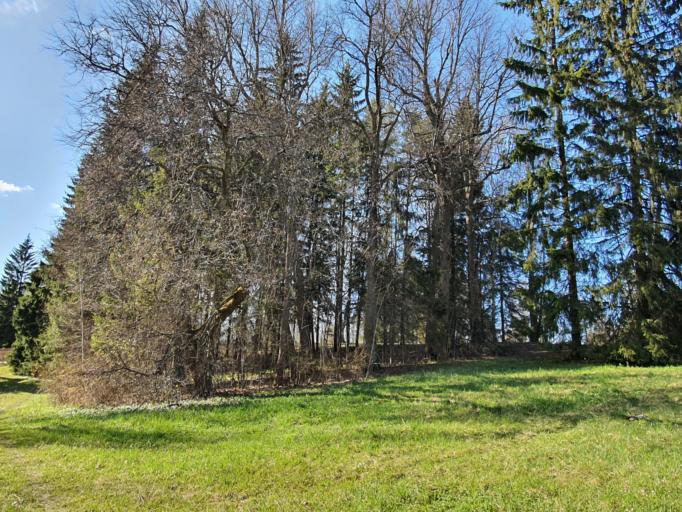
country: RU
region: St.-Petersburg
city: Tyarlevo
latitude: 59.6875
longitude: 30.4535
